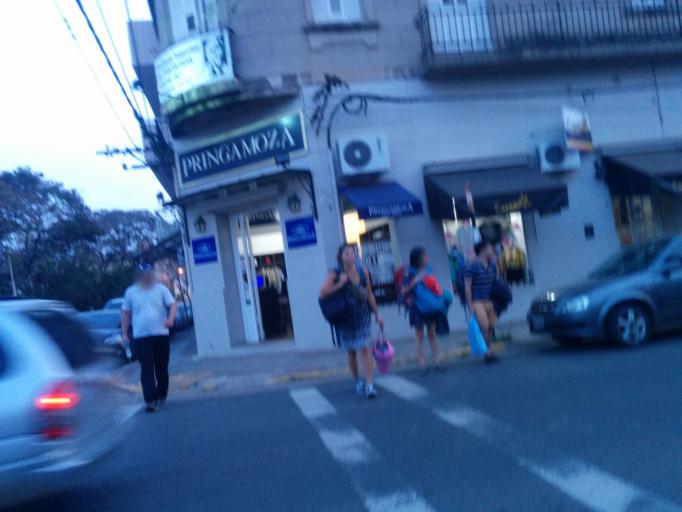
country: AR
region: Entre Rios
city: Concordia
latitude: -31.3913
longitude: -58.0175
